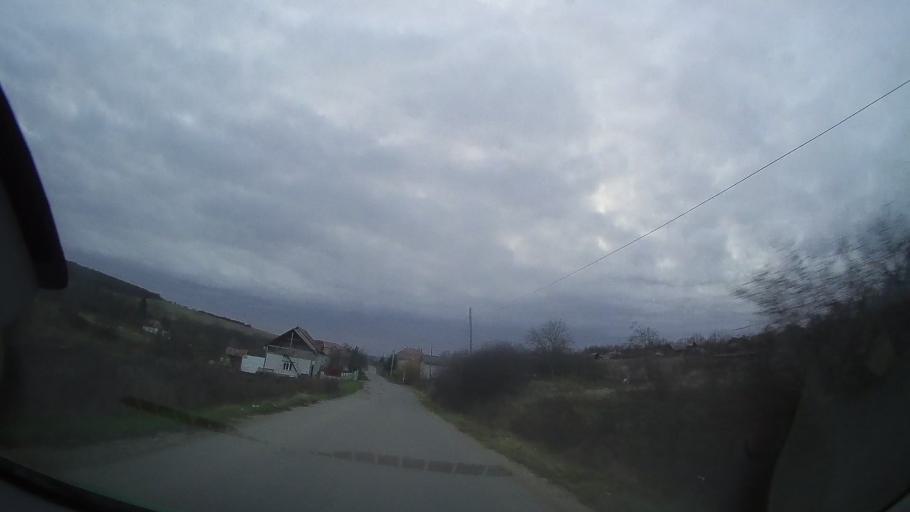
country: RO
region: Cluj
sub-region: Comuna Caianu
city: Vaida-Camaras
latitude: 46.8326
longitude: 23.9567
